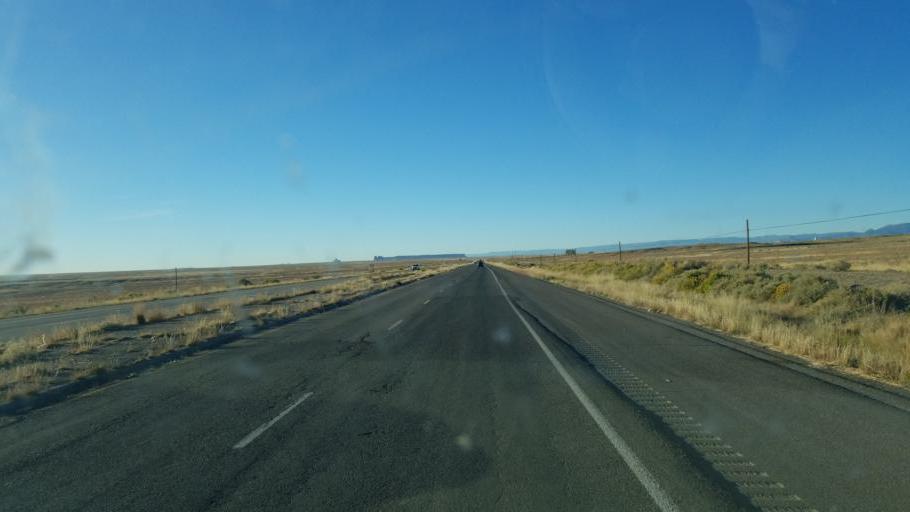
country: US
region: New Mexico
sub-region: San Juan County
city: Shiprock
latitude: 36.7457
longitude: -108.7034
